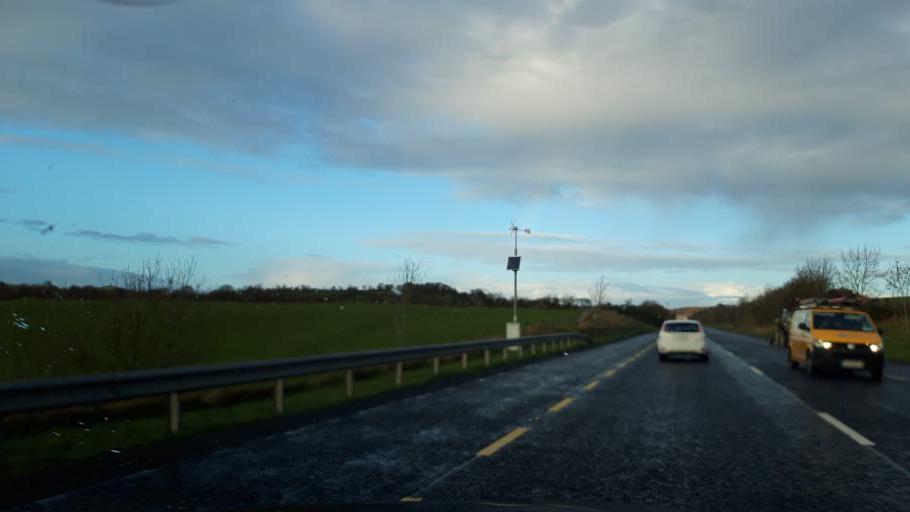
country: IE
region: Ulster
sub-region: County Monaghan
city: Carrickmacross
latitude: 54.0100
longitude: -6.7123
